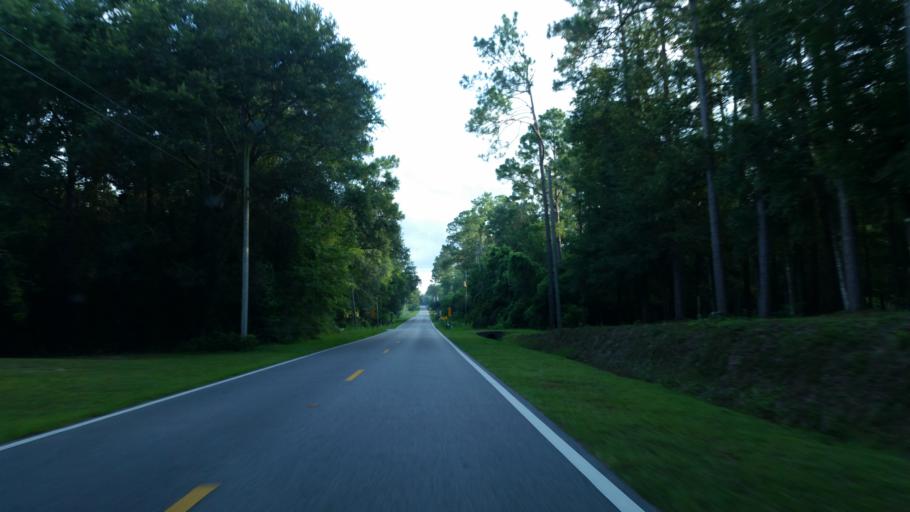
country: US
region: Florida
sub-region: Escambia County
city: Ensley
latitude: 30.5220
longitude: -87.3304
